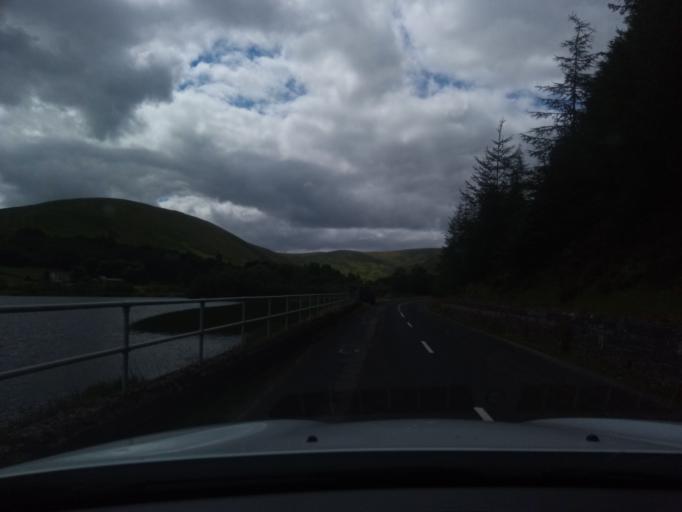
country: GB
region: Scotland
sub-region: The Scottish Borders
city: Peebles
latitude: 55.4628
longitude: -3.2126
